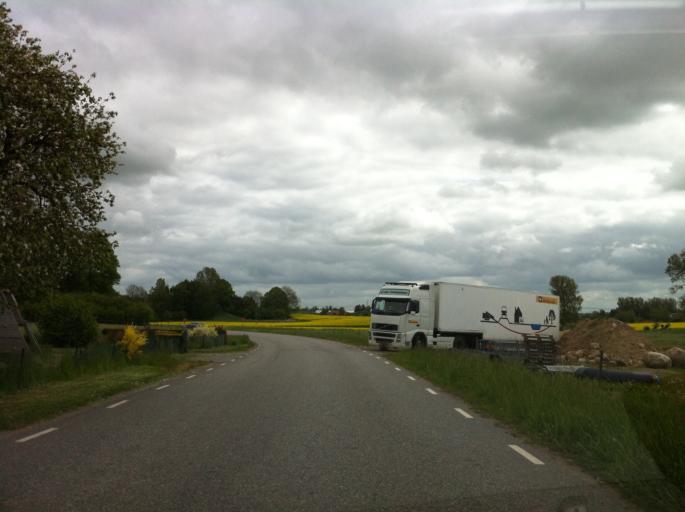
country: SE
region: Skane
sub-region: Kavlinge Kommun
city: Kaevlinge
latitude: 55.8219
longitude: 13.0789
